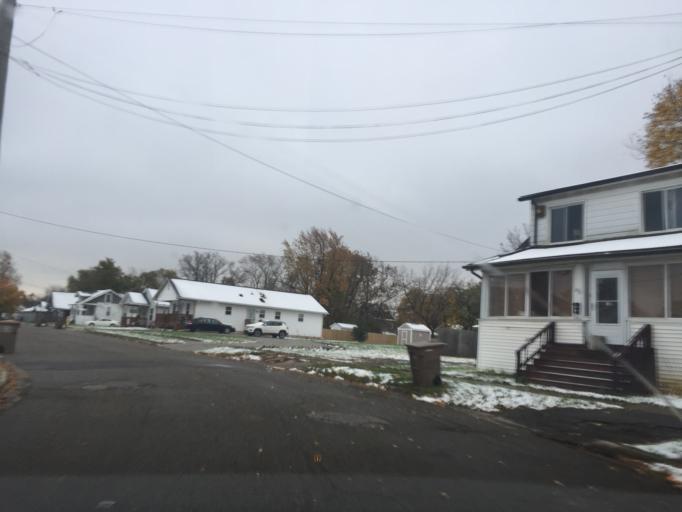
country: US
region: Michigan
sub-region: Oakland County
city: Pontiac
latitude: 42.6225
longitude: -83.2778
